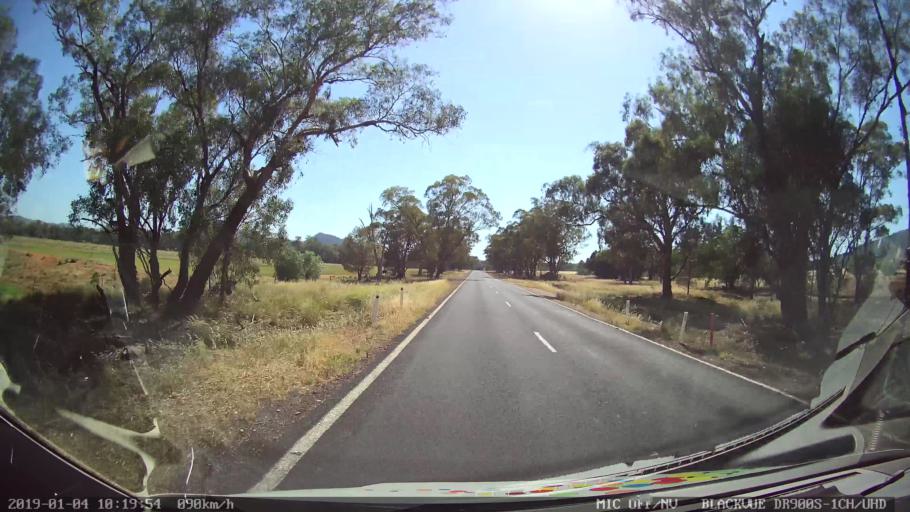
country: AU
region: New South Wales
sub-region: Cabonne
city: Canowindra
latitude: -33.3744
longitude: 148.4877
